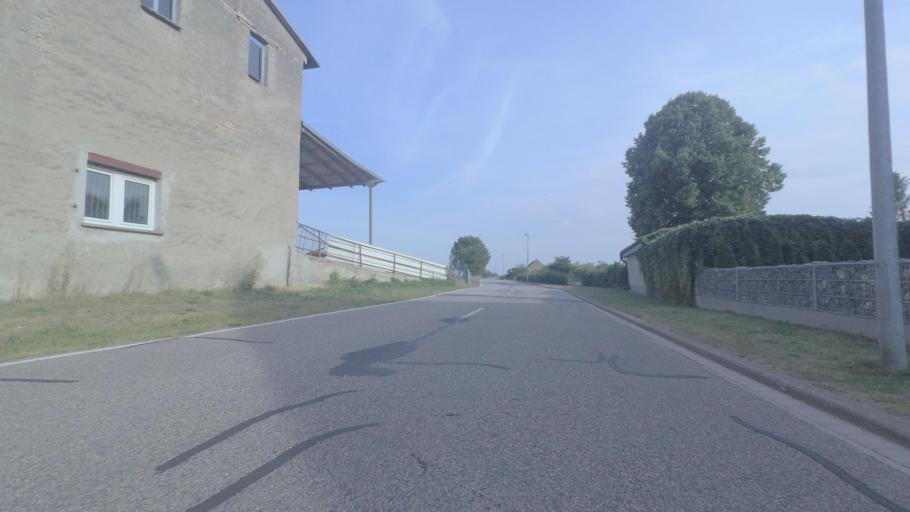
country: DE
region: Mecklenburg-Vorpommern
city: Demmin
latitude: 53.9533
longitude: 13.1113
